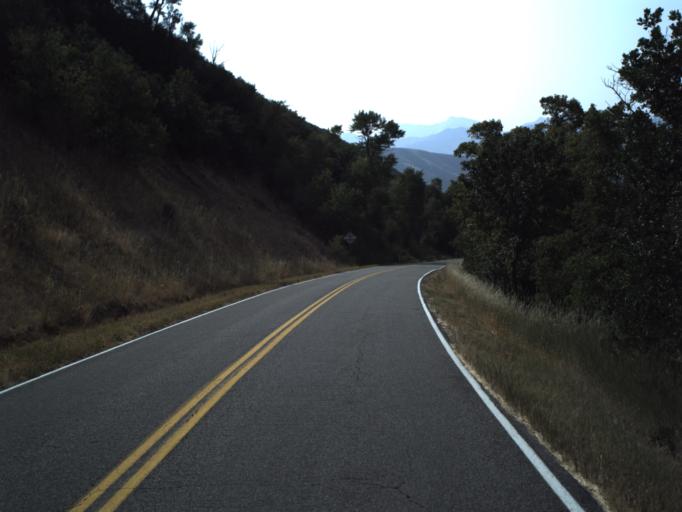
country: US
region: Utah
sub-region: Summit County
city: Summit Park
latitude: 40.8086
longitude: -111.6779
